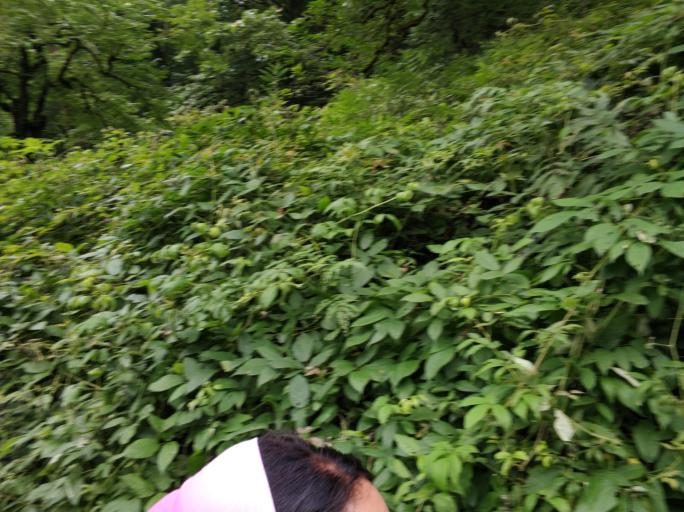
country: IR
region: Gilan
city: Fuman
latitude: 37.0682
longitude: 49.2435
